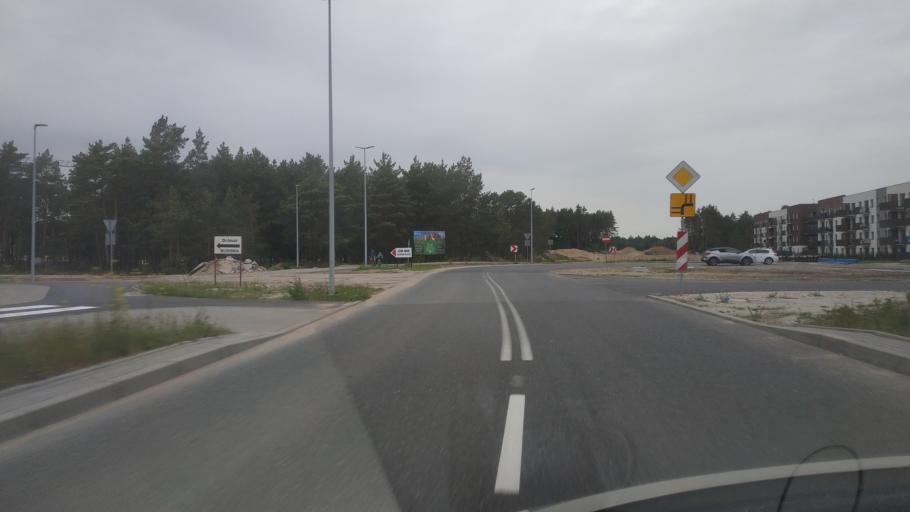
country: PL
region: Kujawsko-Pomorskie
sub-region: Powiat torunski
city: Lysomice
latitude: 53.0521
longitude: 18.6036
